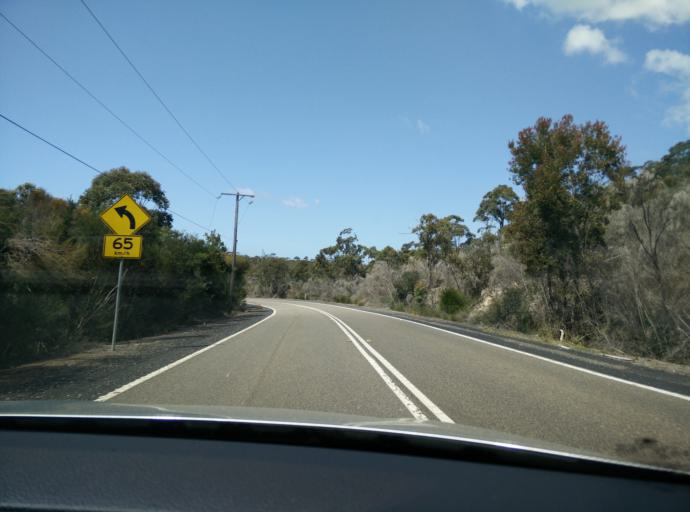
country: AU
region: New South Wales
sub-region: Gosford Shire
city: Blackwall
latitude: -33.4846
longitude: 151.2977
